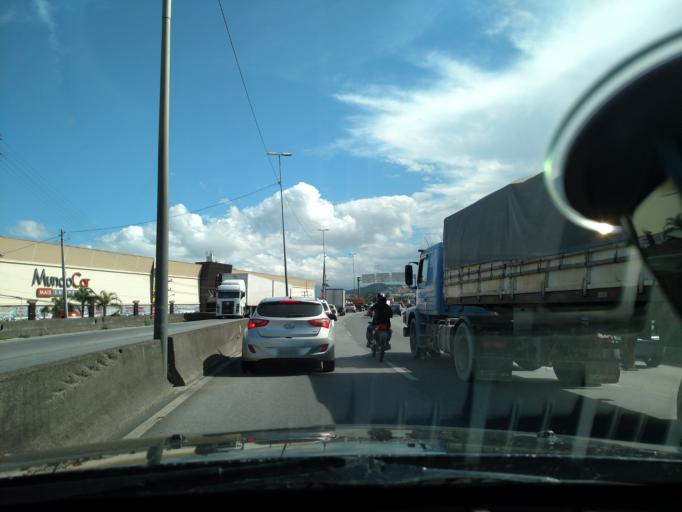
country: BR
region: Santa Catarina
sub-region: Sao Jose
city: Campinas
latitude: -27.5968
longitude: -48.6198
